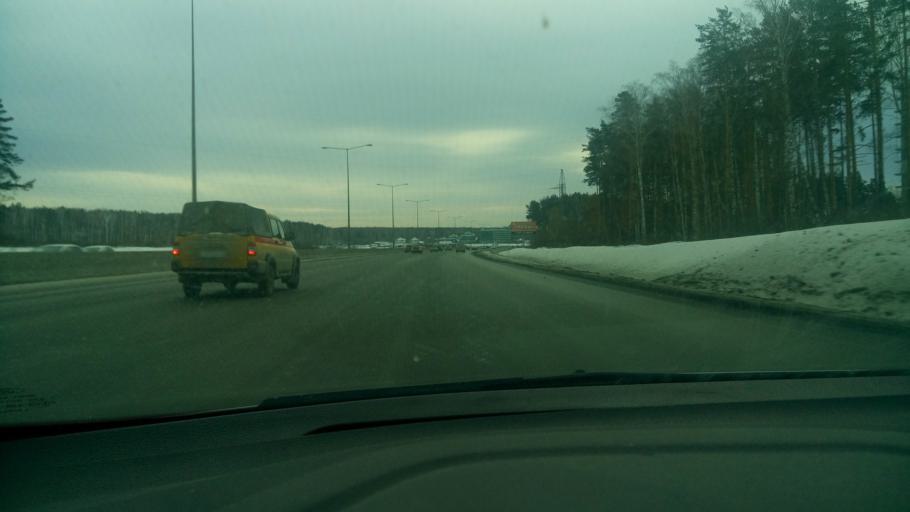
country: RU
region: Sverdlovsk
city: Istok
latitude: 56.7814
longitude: 60.7019
